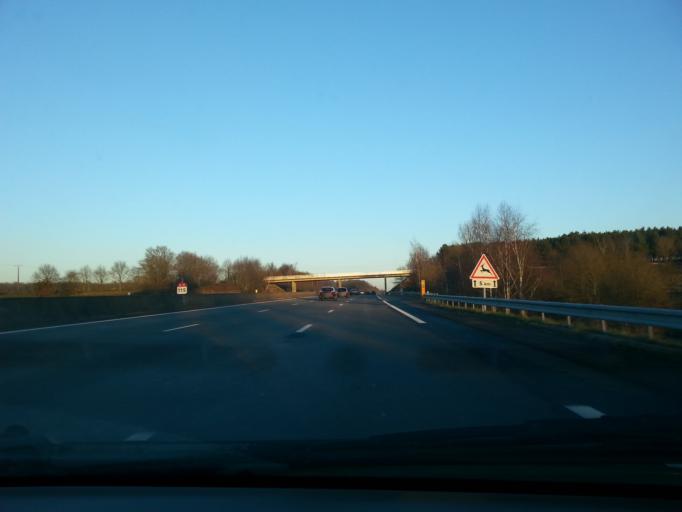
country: FR
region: Centre
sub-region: Departement d'Eure-et-Loir
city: Authon-du-Perche
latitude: 48.1999
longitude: 0.8792
